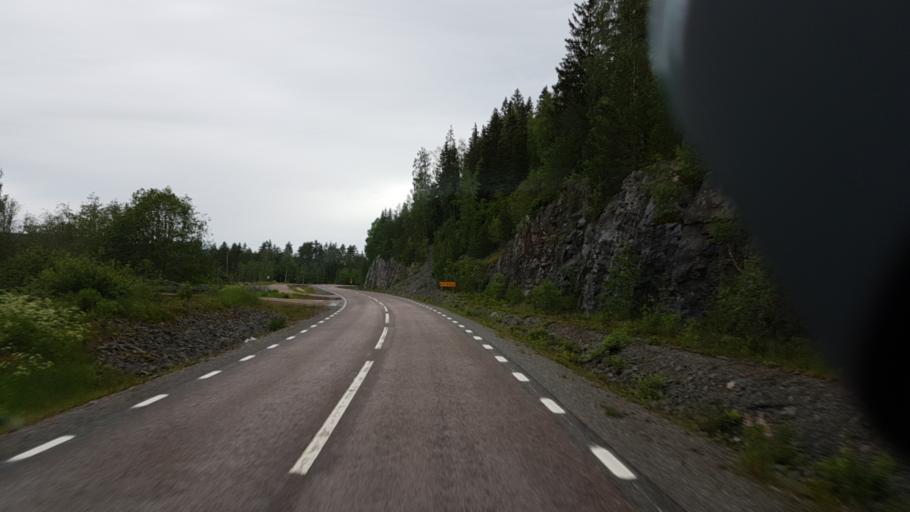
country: SE
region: Vaermland
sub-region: Arjangs Kommun
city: Arjaeng
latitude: 59.6140
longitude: 12.1491
